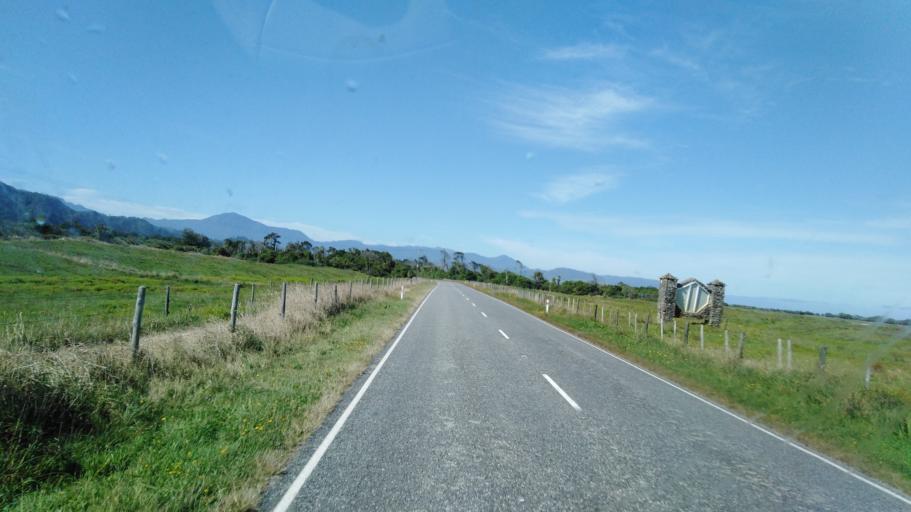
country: NZ
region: West Coast
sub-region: Buller District
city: Westport
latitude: -41.2959
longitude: 172.0930
